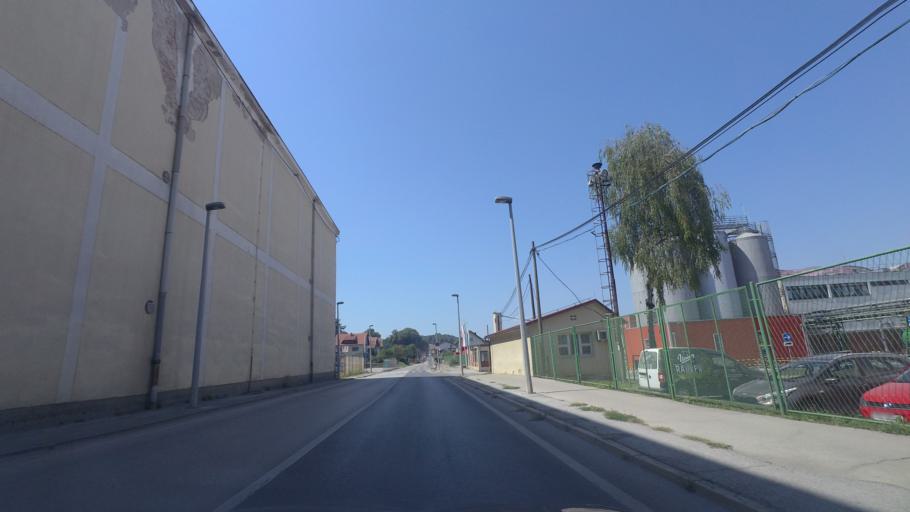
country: HR
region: Karlovacka
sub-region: Grad Karlovac
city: Karlovac
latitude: 45.4983
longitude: 15.5288
